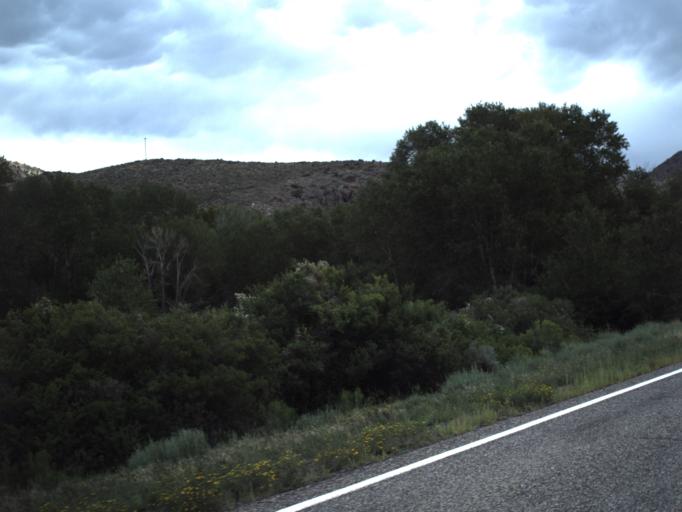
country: US
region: Utah
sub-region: Piute County
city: Junction
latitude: 38.2016
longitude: -112.1732
